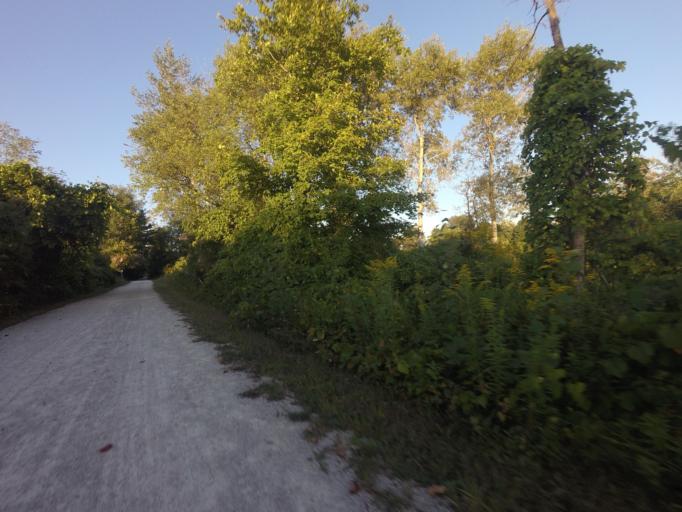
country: CA
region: Ontario
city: Brampton
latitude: 43.8797
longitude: -79.8512
